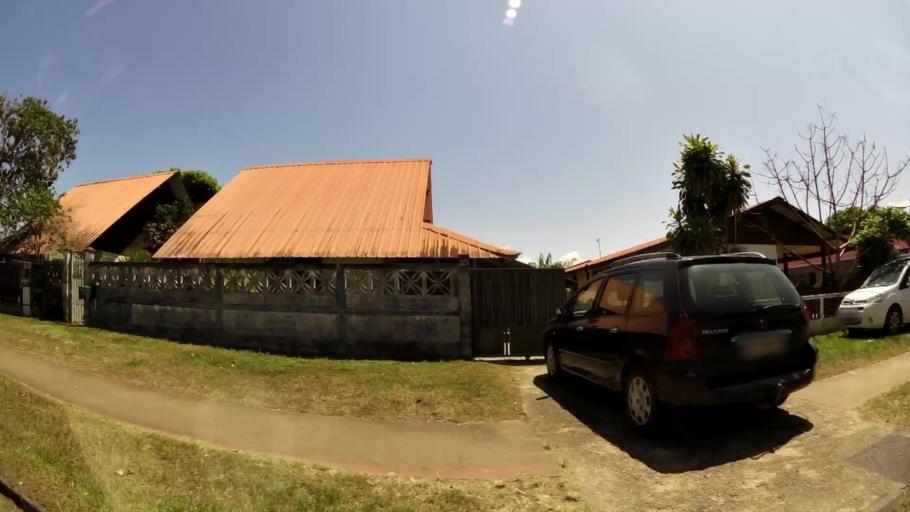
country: GF
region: Guyane
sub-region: Guyane
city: Kourou
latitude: 5.1688
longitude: -52.6540
